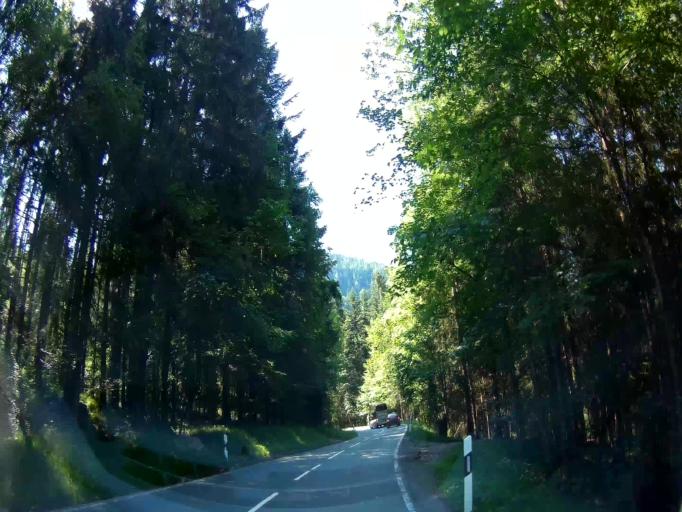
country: DE
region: Bavaria
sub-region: Upper Bavaria
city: Marktschellenberg
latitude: 47.6435
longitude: 13.0596
